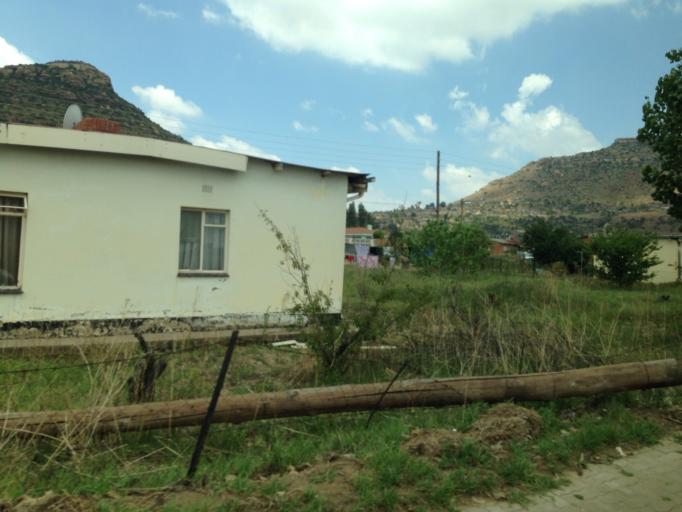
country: LS
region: Maseru
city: Maseru
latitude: -29.3292
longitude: 27.4865
